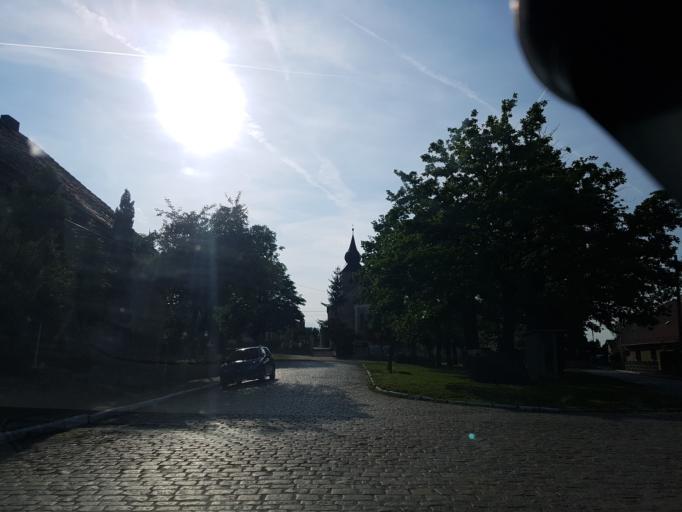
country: PL
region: Lower Silesian Voivodeship
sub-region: Powiat strzelinski
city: Wiazow
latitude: 50.8427
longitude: 17.2108
